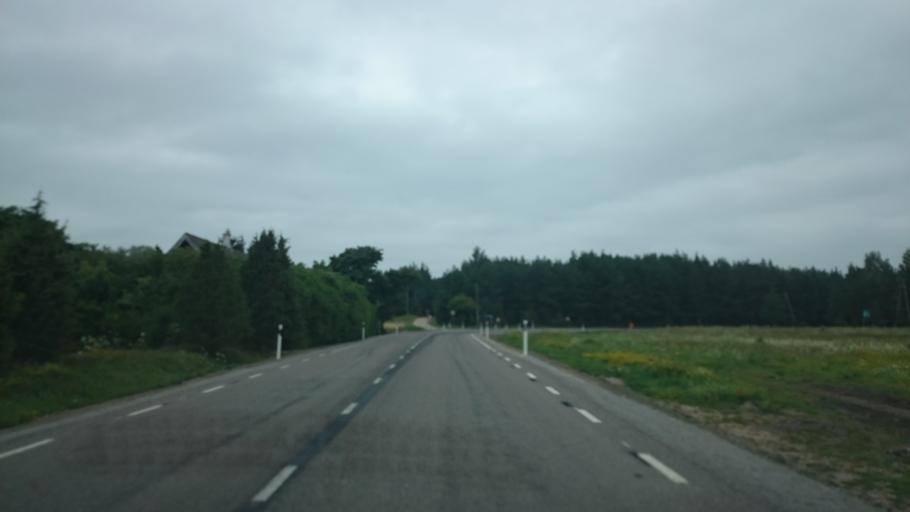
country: EE
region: Saare
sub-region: Orissaare vald
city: Orissaare
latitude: 58.5871
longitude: 22.7058
